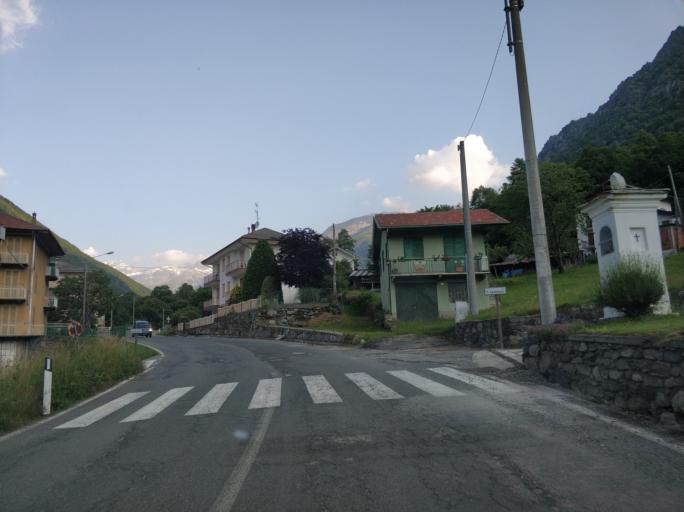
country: IT
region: Piedmont
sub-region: Provincia di Torino
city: Cantoira
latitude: 45.3465
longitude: 7.3742
